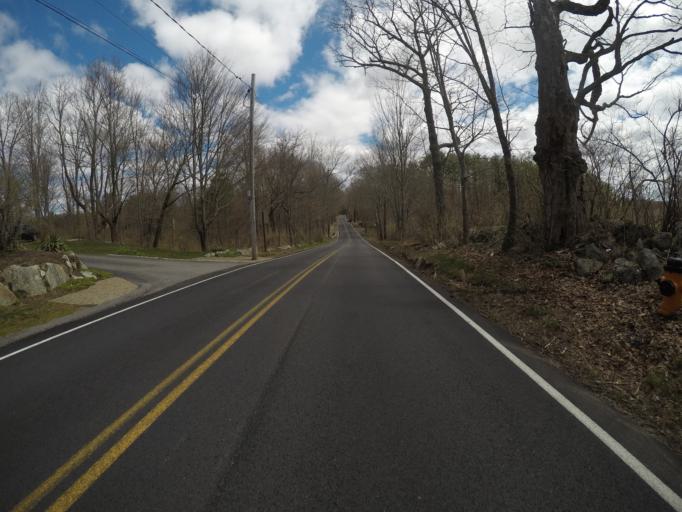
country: US
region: Massachusetts
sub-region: Norfolk County
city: Stoughton
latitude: 42.0766
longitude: -71.0805
